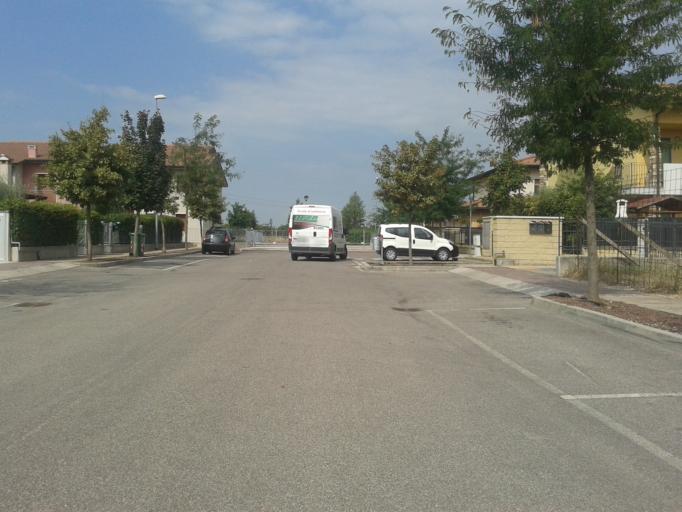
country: IT
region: Veneto
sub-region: Provincia di Verona
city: Mozzecane
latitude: 45.3082
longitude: 10.8092
